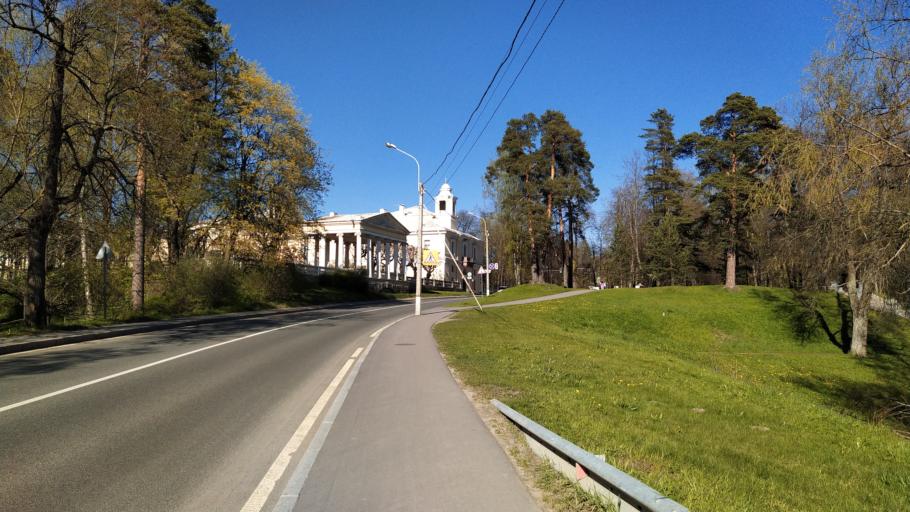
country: RU
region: St.-Petersburg
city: Pavlovsk
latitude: 59.6843
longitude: 30.4516
